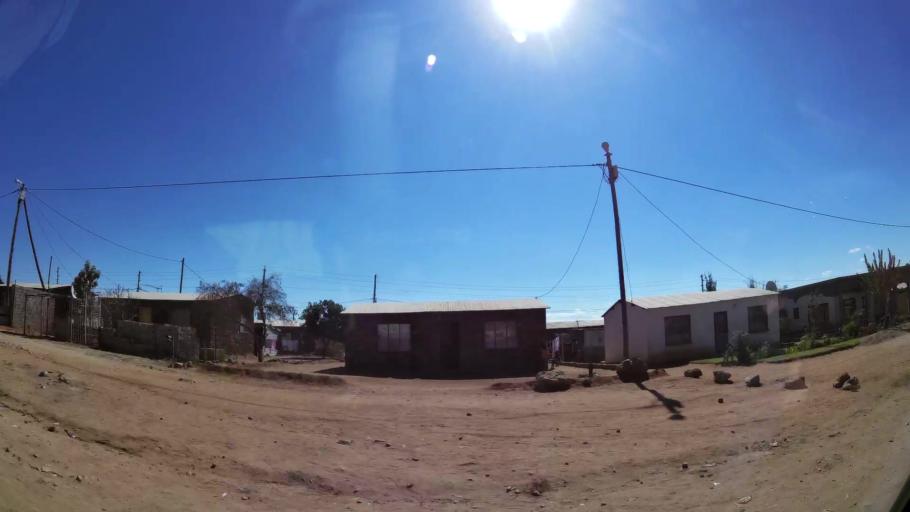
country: ZA
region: Limpopo
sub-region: Capricorn District Municipality
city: Polokwane
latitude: -23.8907
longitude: 29.4142
